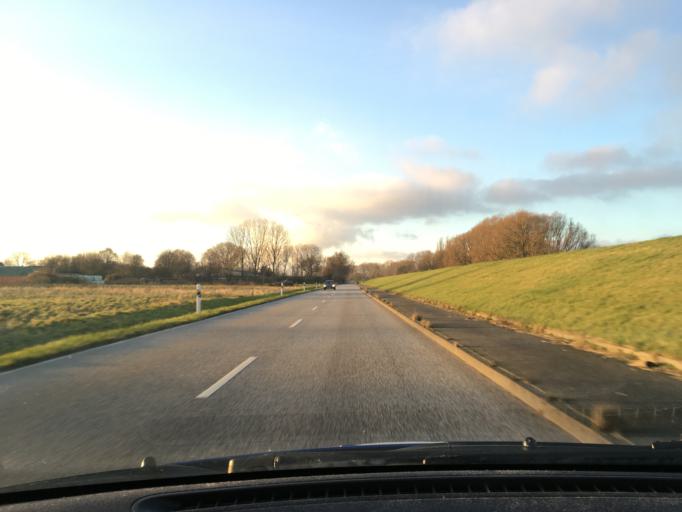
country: DE
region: Hamburg
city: Harburg
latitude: 53.4679
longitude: 10.0422
